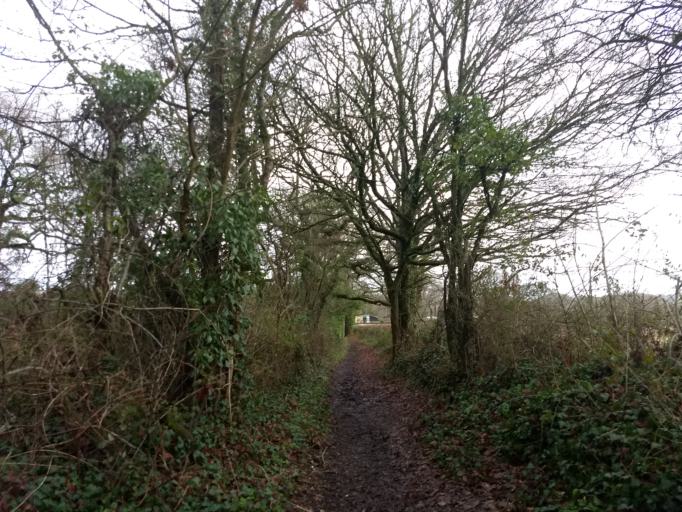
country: GB
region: England
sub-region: Isle of Wight
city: Newport
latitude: 50.7157
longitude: -1.2403
